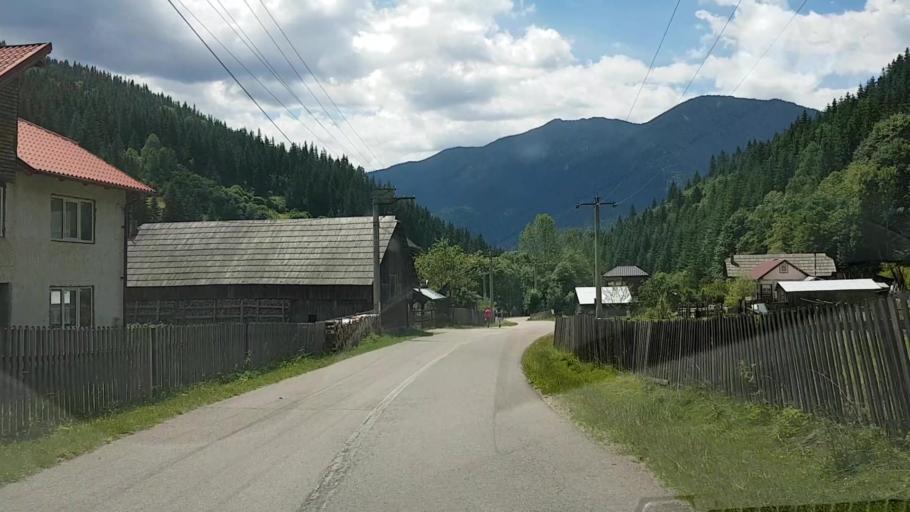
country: RO
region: Suceava
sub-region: Comuna Crucea
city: Crucea
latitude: 47.4142
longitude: 25.5840
